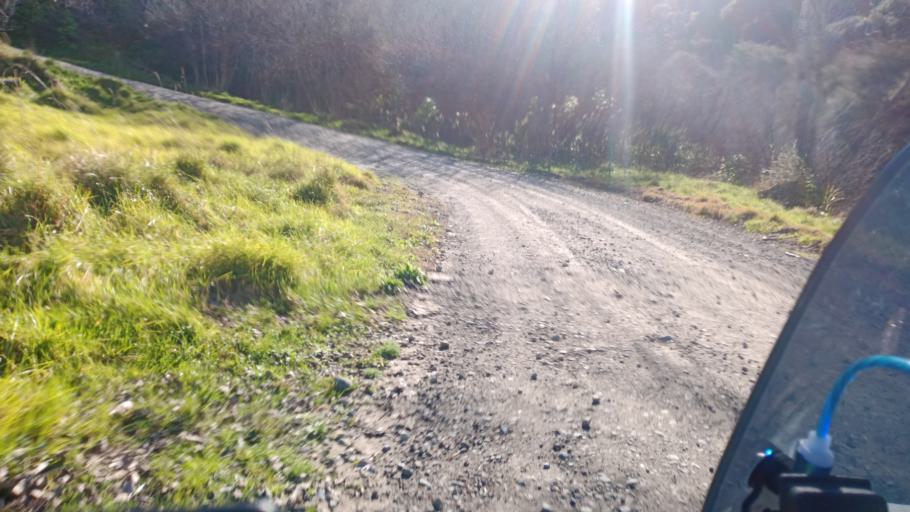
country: NZ
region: Gisborne
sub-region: Gisborne District
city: Gisborne
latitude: -38.2277
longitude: 178.3110
